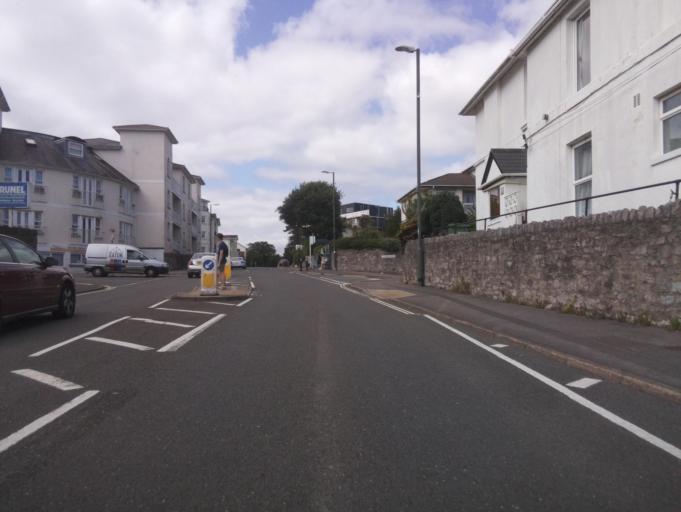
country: GB
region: England
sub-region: Borough of Torbay
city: Torquay
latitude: 50.4795
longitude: -3.5167
